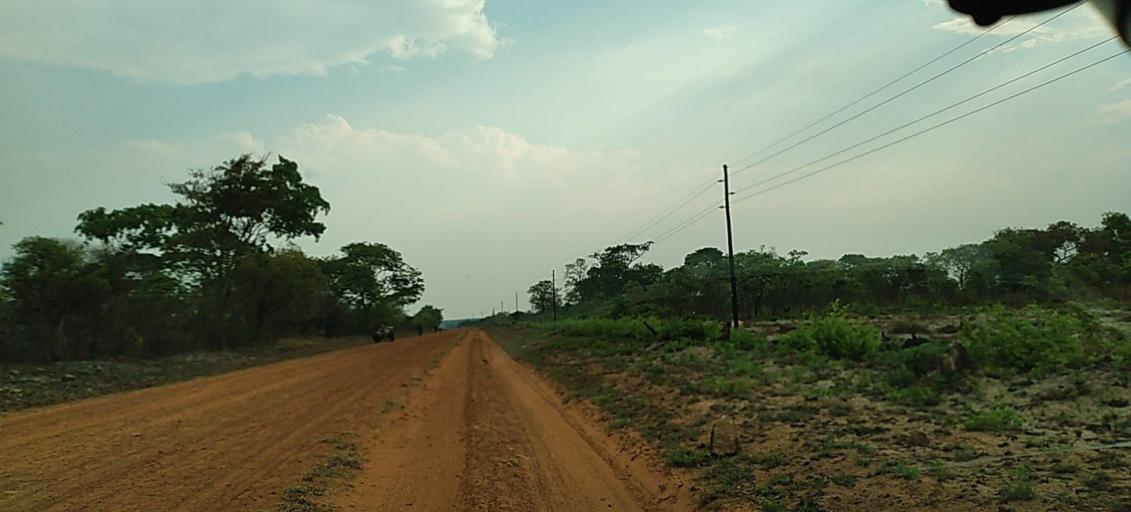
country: ZM
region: Western
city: Lukulu
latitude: -13.9028
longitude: 23.6548
